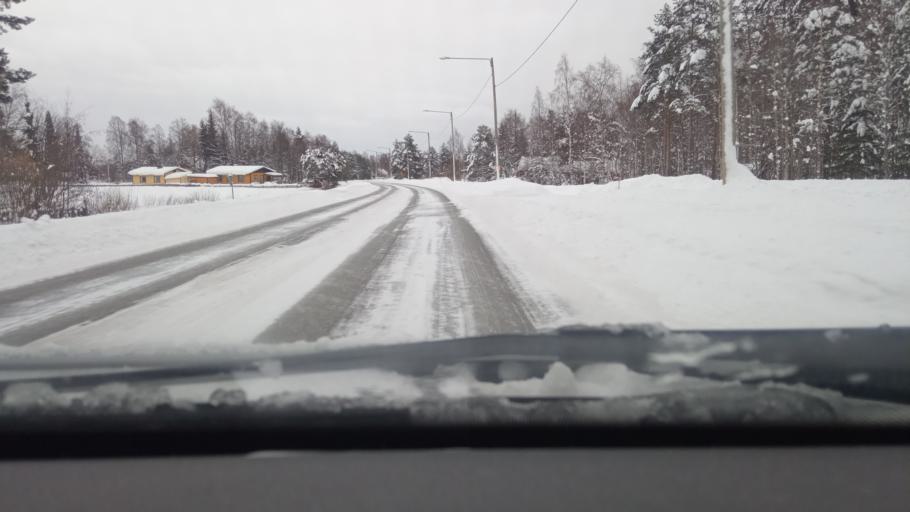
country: FI
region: Southern Ostrobothnia
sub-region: Jaerviseutu
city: Alajaervi
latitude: 62.9935
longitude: 23.8267
